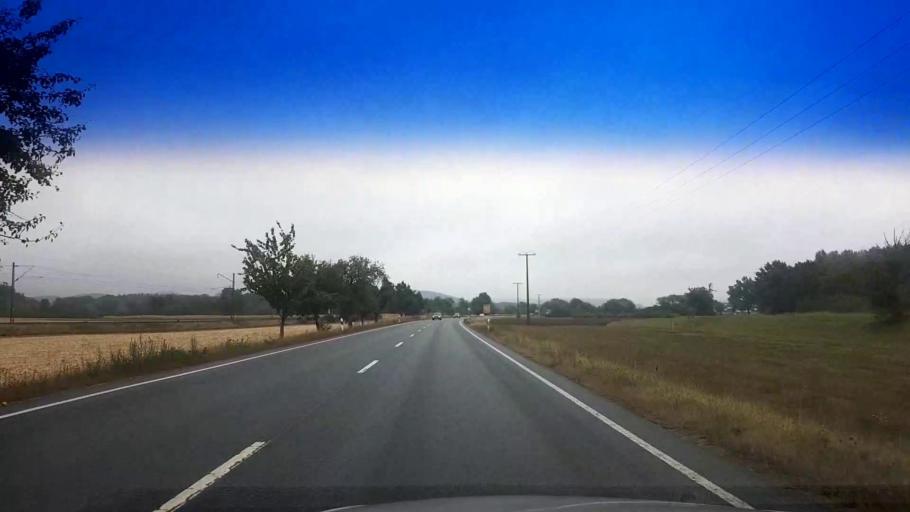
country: DE
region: Bavaria
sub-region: Upper Franconia
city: Eggolsheim
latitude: 49.7592
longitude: 11.0500
